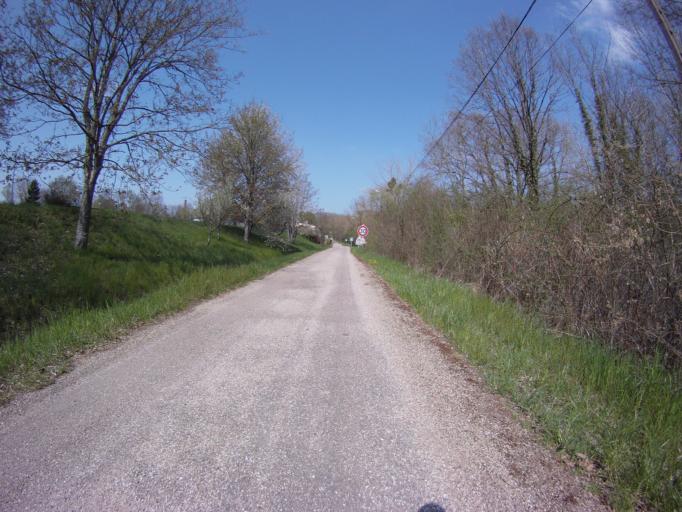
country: FR
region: Lorraine
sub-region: Departement de Meurthe-et-Moselle
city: Blenod-les-Pont-a-Mousson
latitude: 48.8707
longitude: 6.0721
